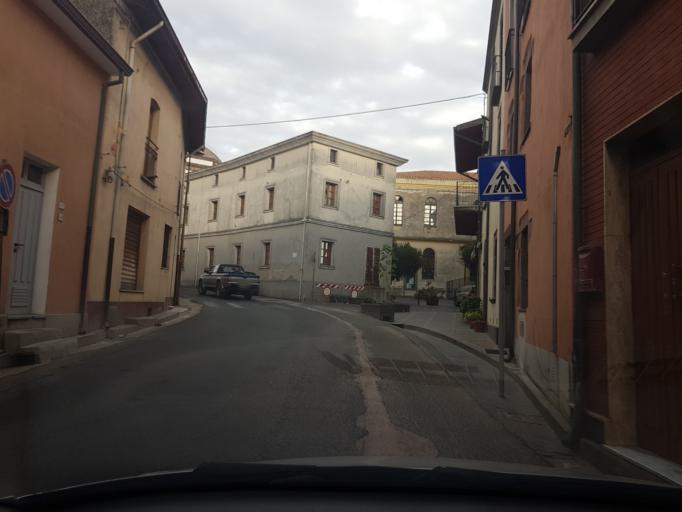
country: IT
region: Sardinia
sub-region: Provincia di Oristano
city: Seneghe
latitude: 40.0810
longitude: 8.6110
